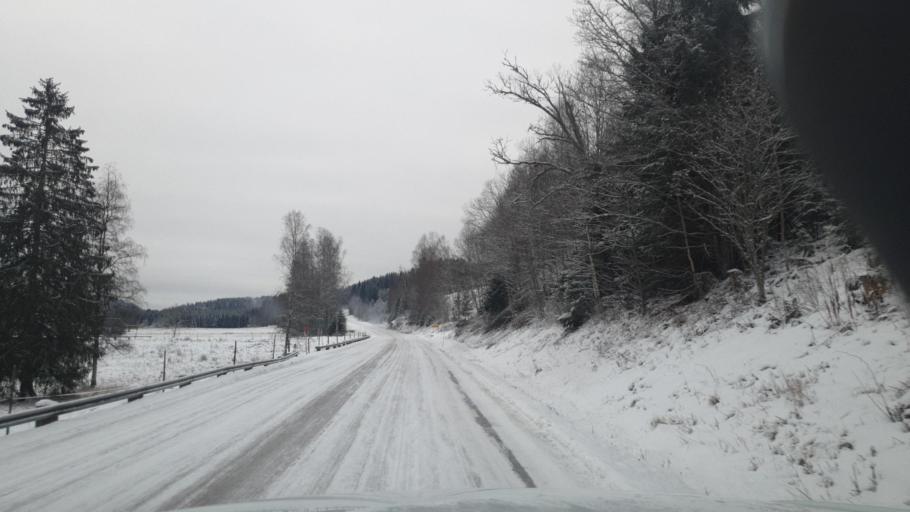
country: NO
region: Hedmark
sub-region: Eidskog
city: Skotterud
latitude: 59.7752
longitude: 12.0465
